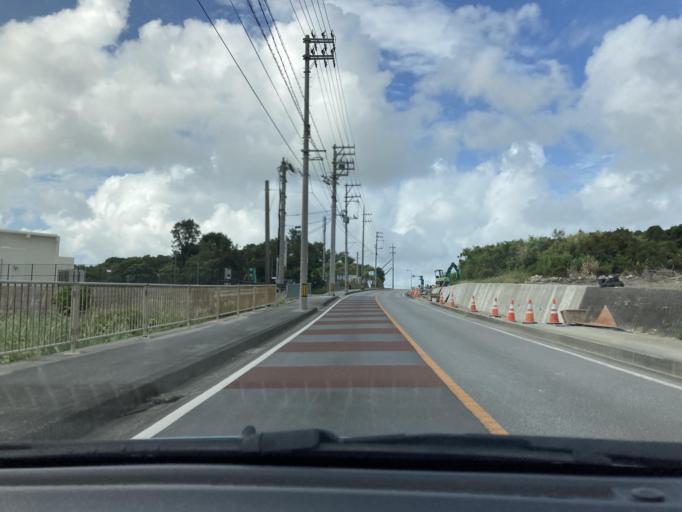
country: JP
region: Okinawa
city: Itoman
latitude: 26.1081
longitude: 127.6944
